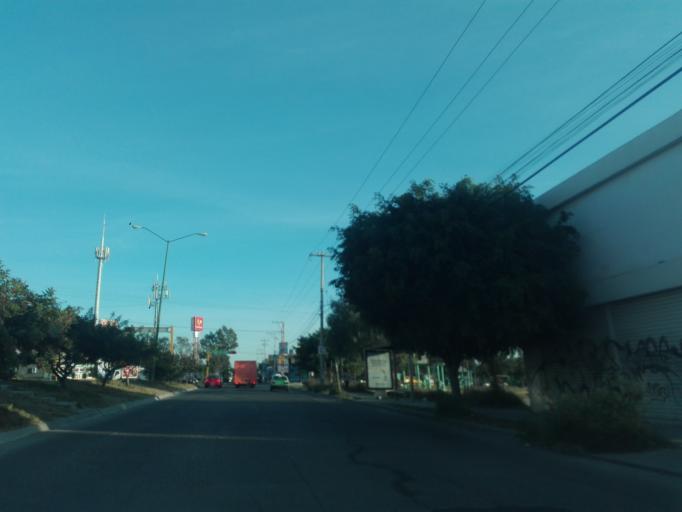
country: MX
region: Guanajuato
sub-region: Leon
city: San Jose de Duran (Los Troncoso)
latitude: 21.0845
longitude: -101.6442
